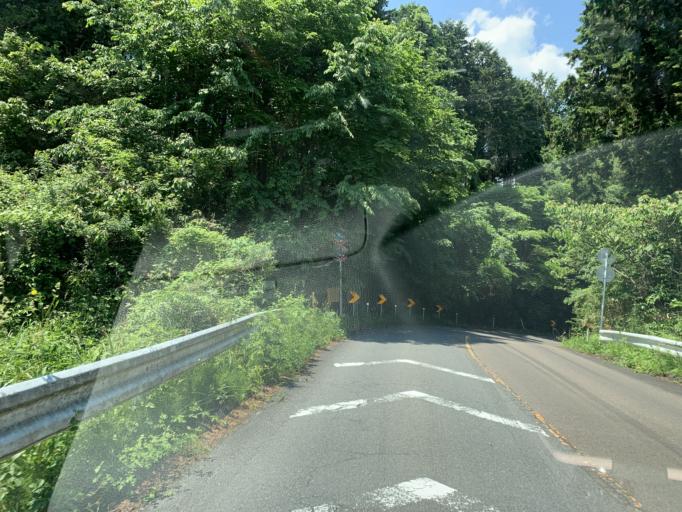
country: JP
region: Miyagi
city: Matsushima
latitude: 38.3677
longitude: 141.0507
